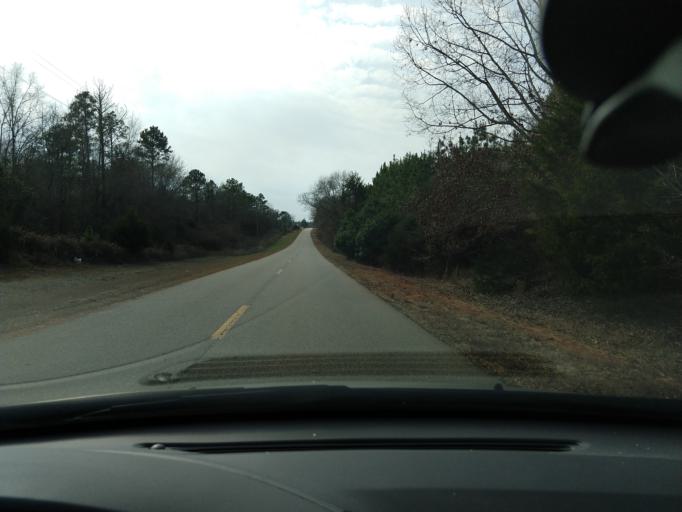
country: US
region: Georgia
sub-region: Webster County
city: Preston
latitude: 32.0306
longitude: -84.4179
